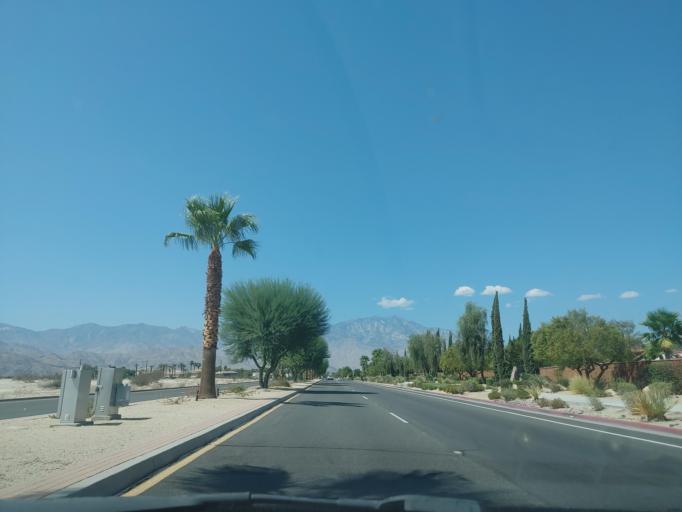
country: US
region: California
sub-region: Riverside County
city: Thousand Palms
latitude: 33.7872
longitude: -116.4014
